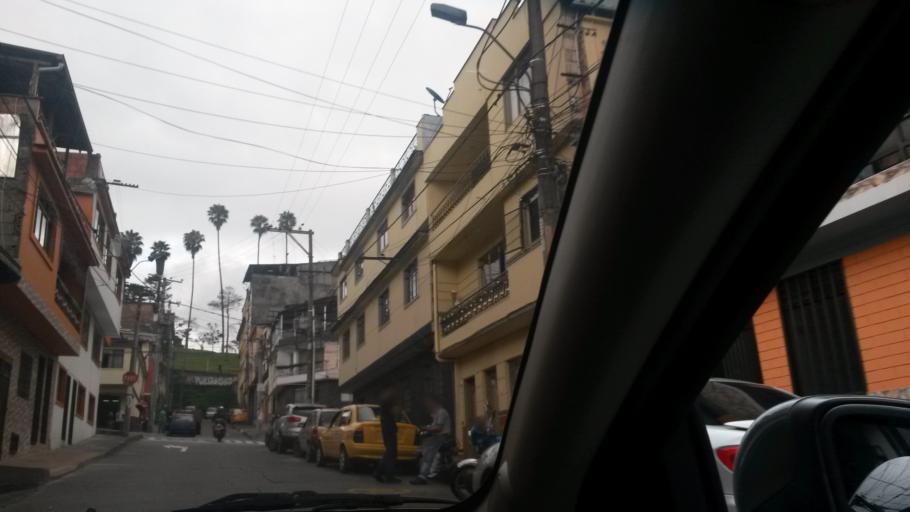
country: CO
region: Caldas
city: Manizales
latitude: 5.0663
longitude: -75.5097
